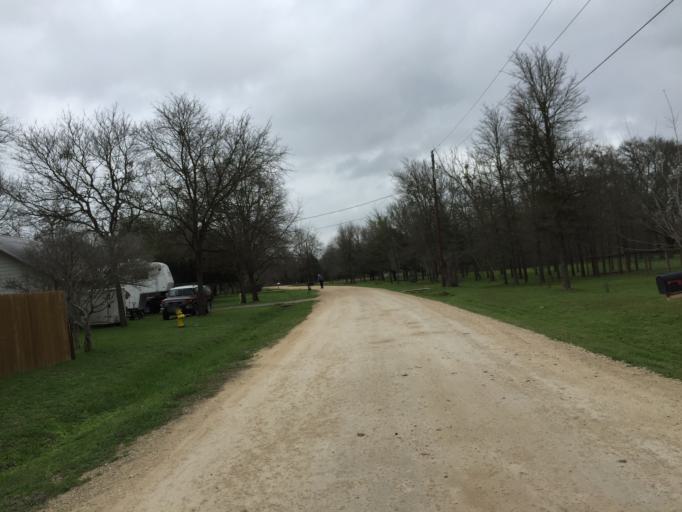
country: US
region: Texas
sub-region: Bastrop County
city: Bastrop
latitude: 30.0827
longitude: -97.3248
